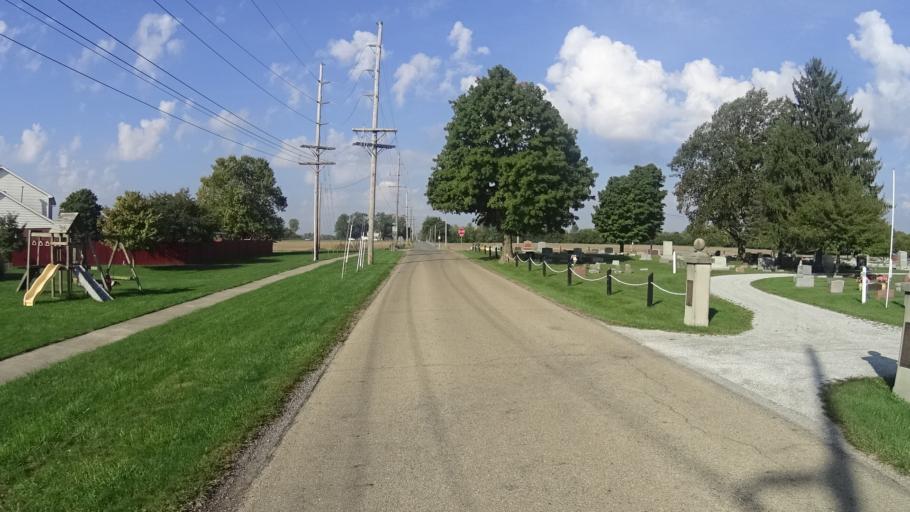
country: US
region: Indiana
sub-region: Madison County
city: Lapel
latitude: 40.0600
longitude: -85.8526
